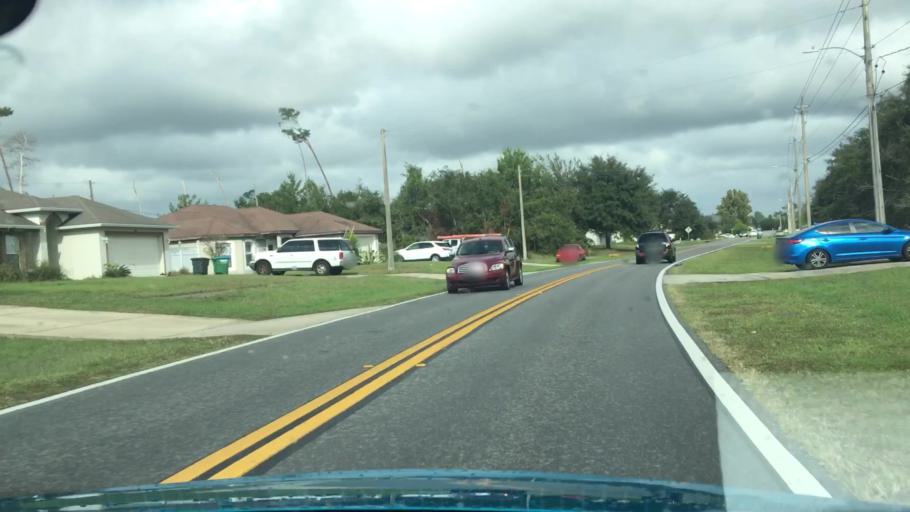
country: US
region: Florida
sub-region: Volusia County
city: Lake Helen
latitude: 28.9360
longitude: -81.1791
